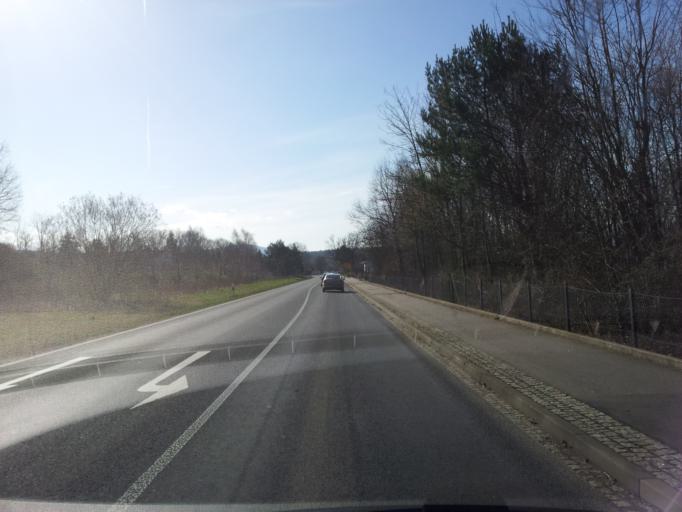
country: DE
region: Saxony
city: Konigsbruck
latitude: 51.2716
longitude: 13.9094
